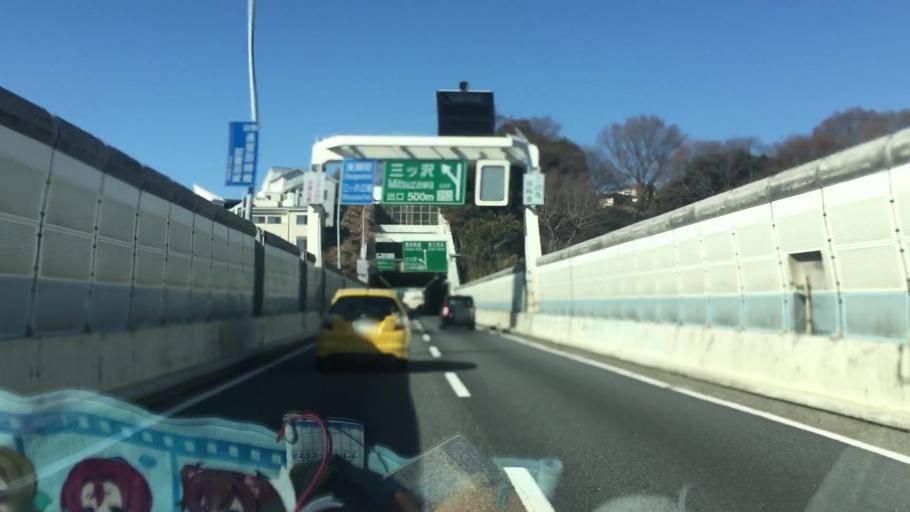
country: JP
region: Kanagawa
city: Yokohama
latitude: 35.4693
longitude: 139.6145
